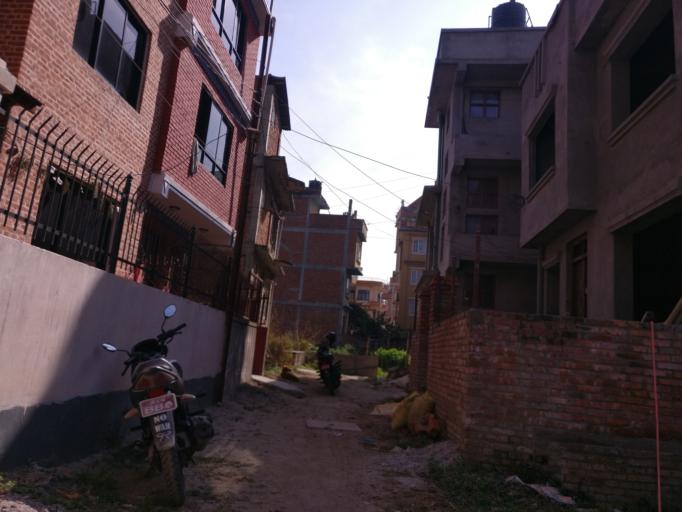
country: NP
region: Central Region
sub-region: Bagmati Zone
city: Patan
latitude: 27.6779
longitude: 85.3310
